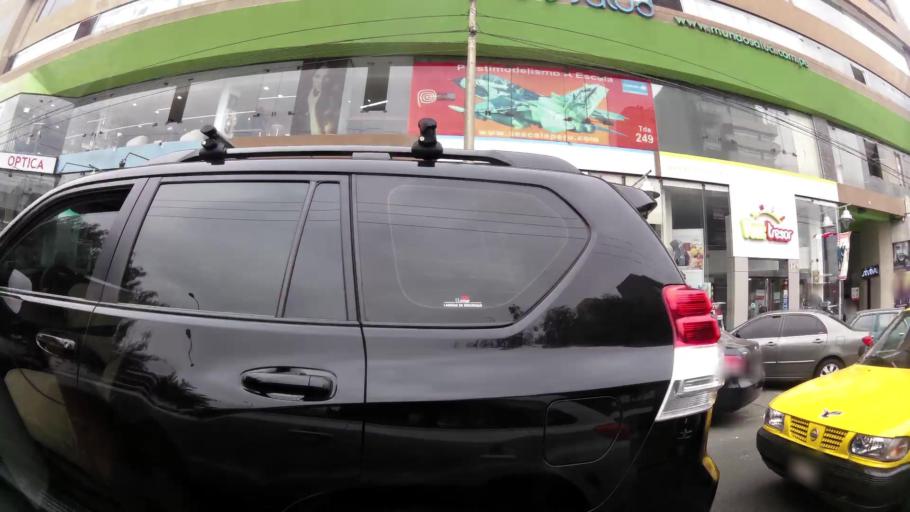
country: PE
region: Lima
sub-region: Lima
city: Surco
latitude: -12.1139
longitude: -76.9919
